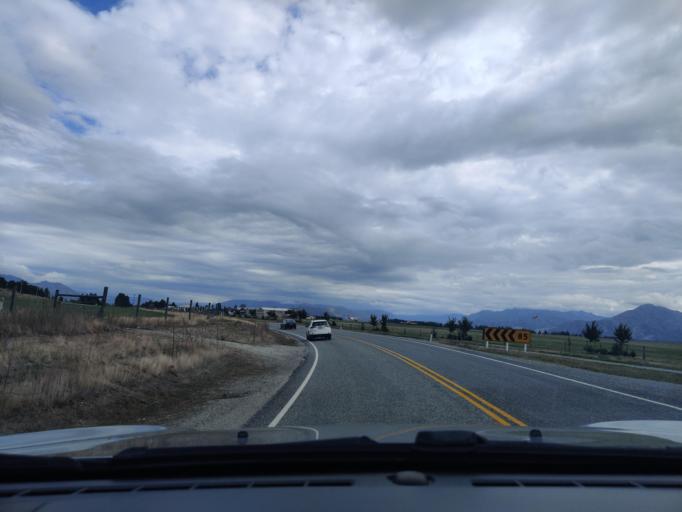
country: NZ
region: Otago
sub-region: Queenstown-Lakes District
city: Wanaka
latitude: -44.7277
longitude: 169.2512
